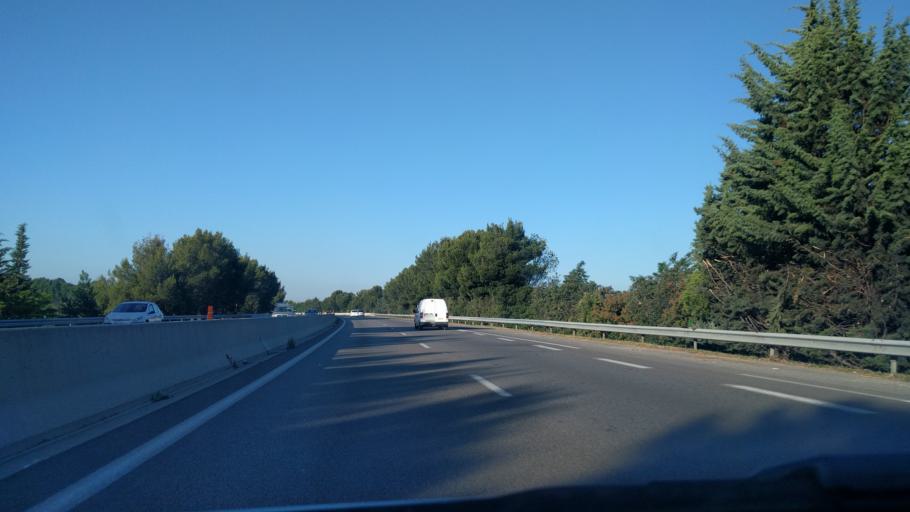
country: FR
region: Provence-Alpes-Cote d'Azur
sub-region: Departement des Bouches-du-Rhone
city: Venelles
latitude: 43.5906
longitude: 5.4806
